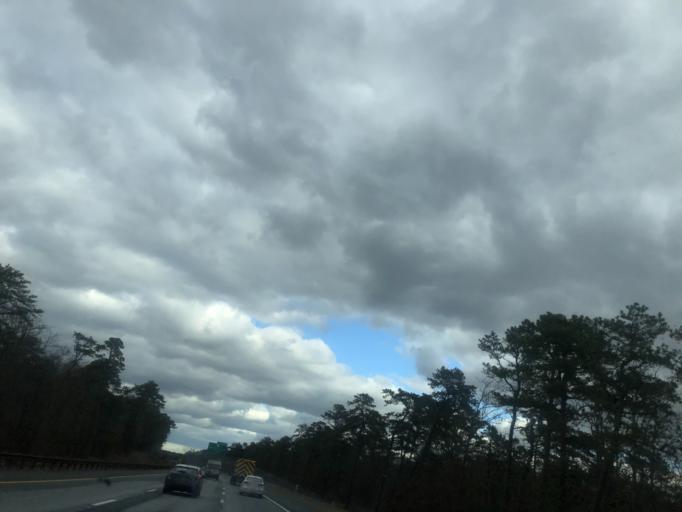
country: US
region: New Jersey
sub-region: Ocean County
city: Manahawkin
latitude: 39.6813
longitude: -74.3039
